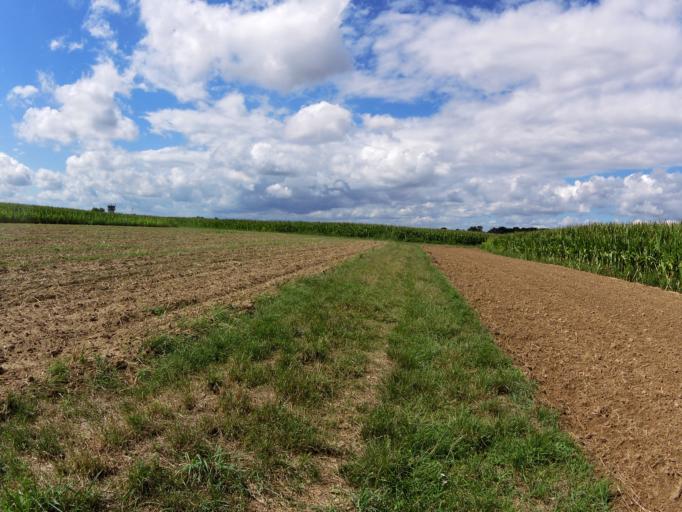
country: DE
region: Baden-Wuerttemberg
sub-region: Freiburg Region
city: Lahr
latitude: 48.3669
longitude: 7.8321
